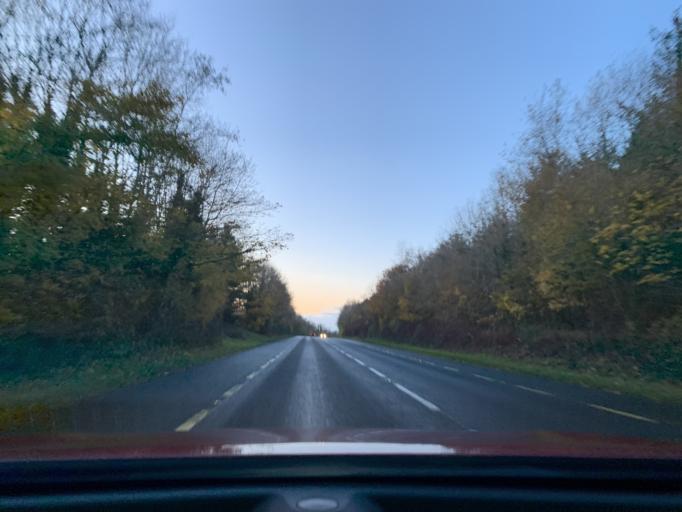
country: IE
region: Connaught
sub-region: County Leitrim
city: Carrick-on-Shannon
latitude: 53.9355
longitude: -8.0515
